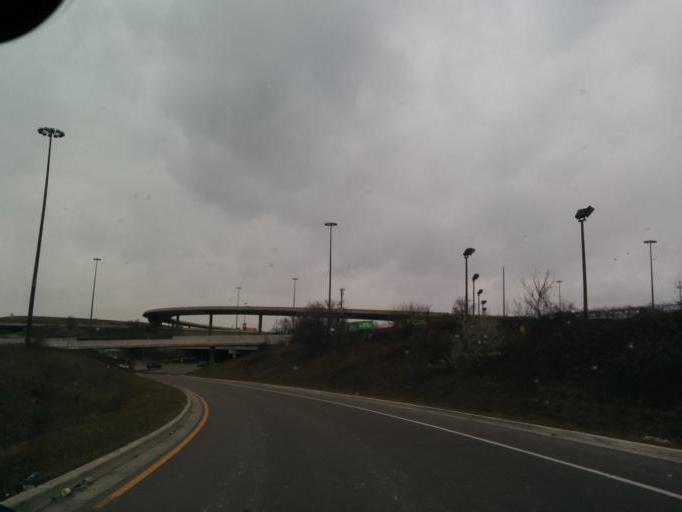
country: CA
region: Ontario
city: Etobicoke
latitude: 43.6119
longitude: -79.5471
